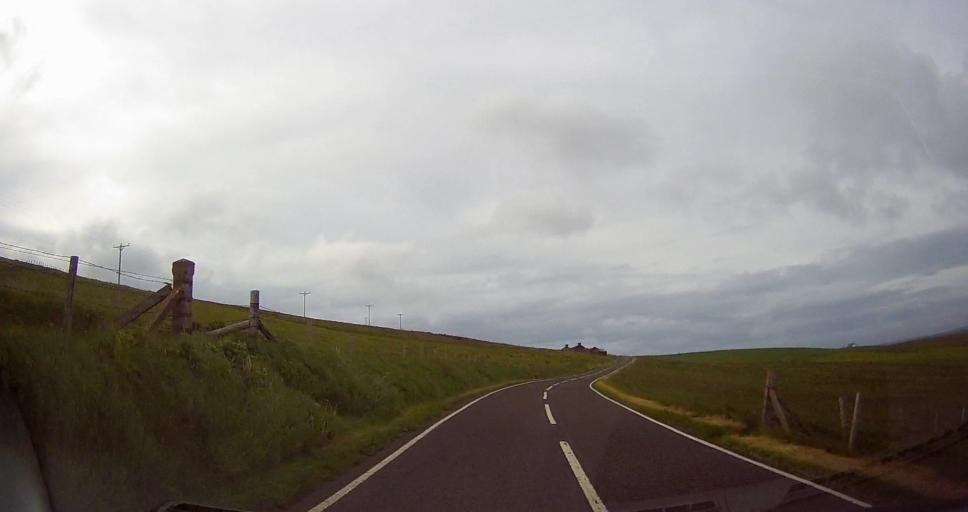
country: GB
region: Scotland
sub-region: Orkney Islands
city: Stromness
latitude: 58.9252
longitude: -3.1995
